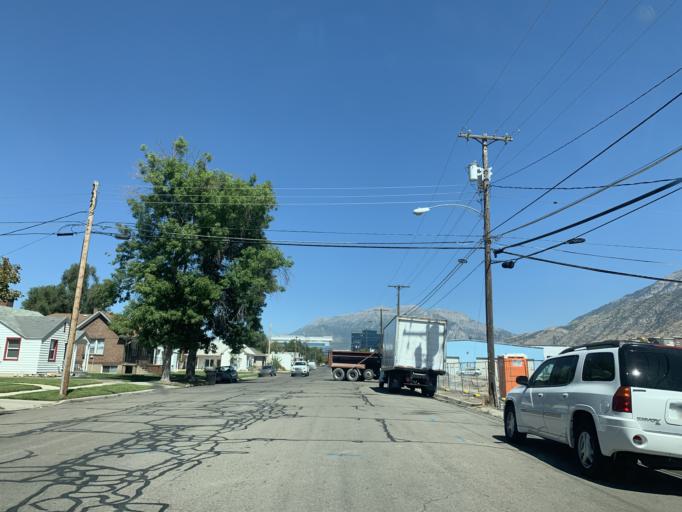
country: US
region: Utah
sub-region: Utah County
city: Provo
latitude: 40.2275
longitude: -111.6605
